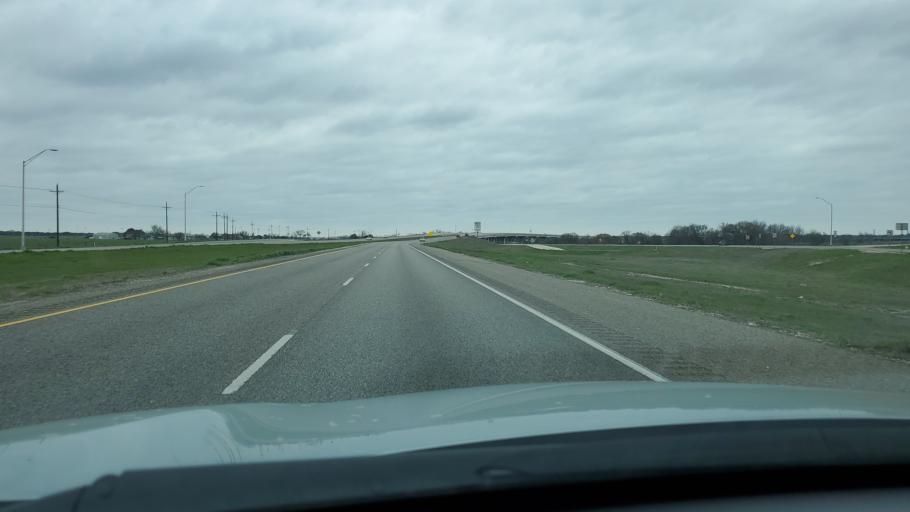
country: US
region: Texas
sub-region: Williamson County
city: Florence
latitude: 30.8189
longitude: -97.7784
